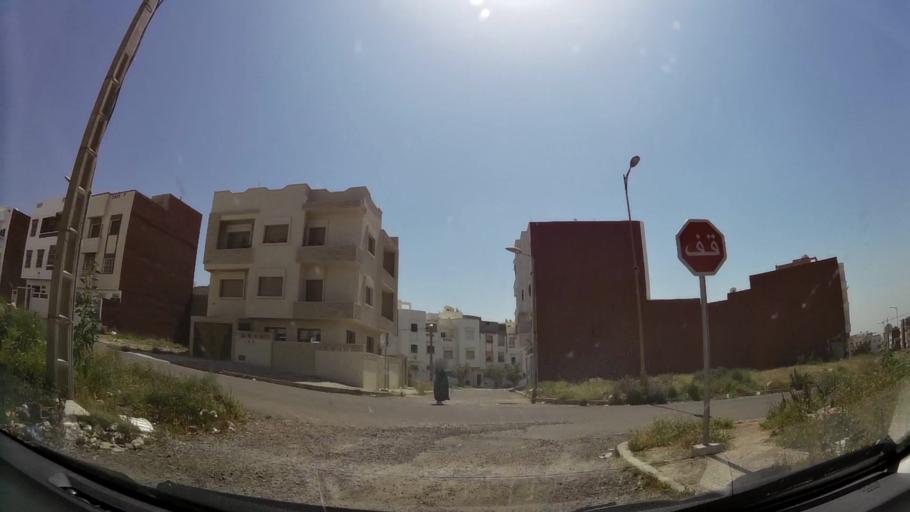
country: MA
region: Oued ed Dahab-Lagouira
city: Dakhla
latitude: 30.4404
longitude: -9.5552
